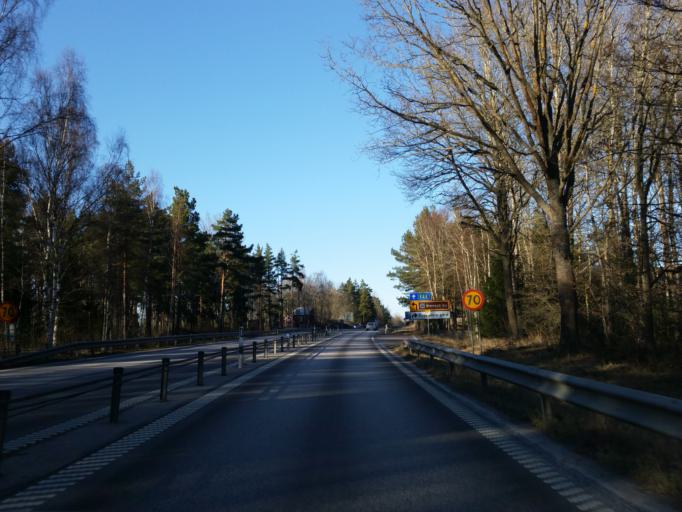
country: SE
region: Kalmar
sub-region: Oskarshamns Kommun
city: Oskarshamn
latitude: 57.3329
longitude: 16.4792
